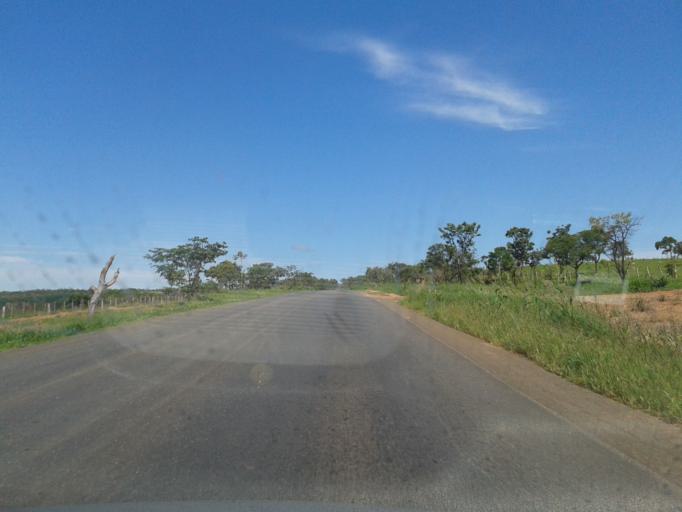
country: BR
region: Goias
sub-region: Bela Vista De Goias
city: Bela Vista de Goias
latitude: -17.1573
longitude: -48.7915
